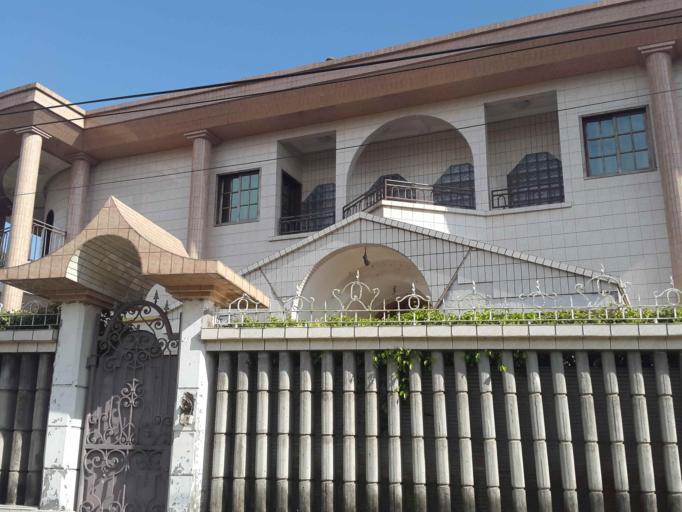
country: CM
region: Littoral
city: Douala
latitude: 4.0901
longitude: 9.7351
